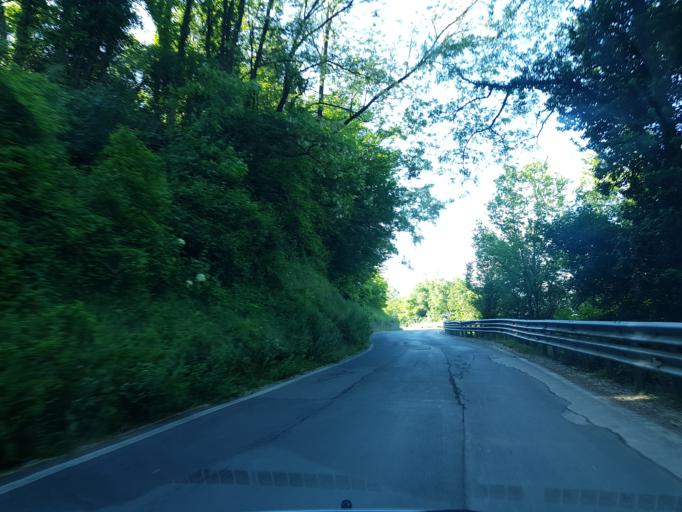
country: IT
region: Tuscany
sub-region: Provincia di Lucca
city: Piazza al Serchio-San Michele
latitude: 44.1983
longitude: 10.2776
